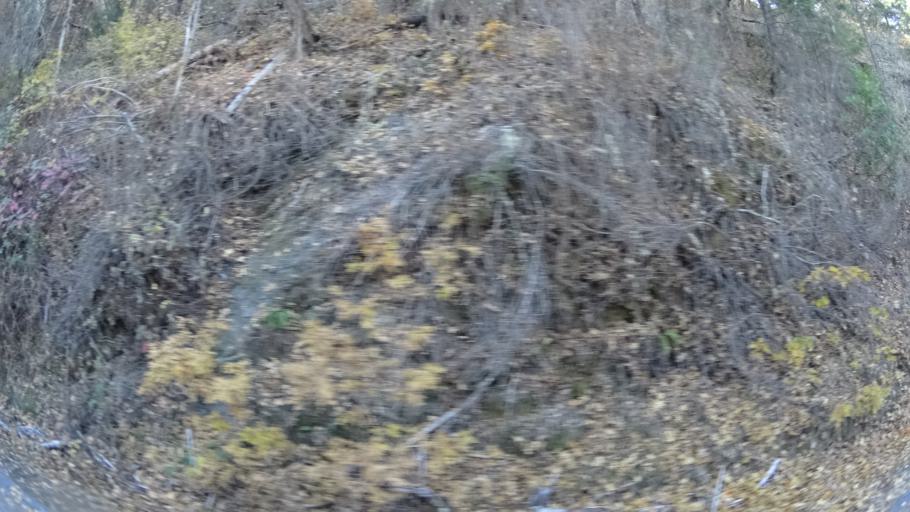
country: US
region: California
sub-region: Siskiyou County
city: Yreka
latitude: 41.8428
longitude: -122.8997
